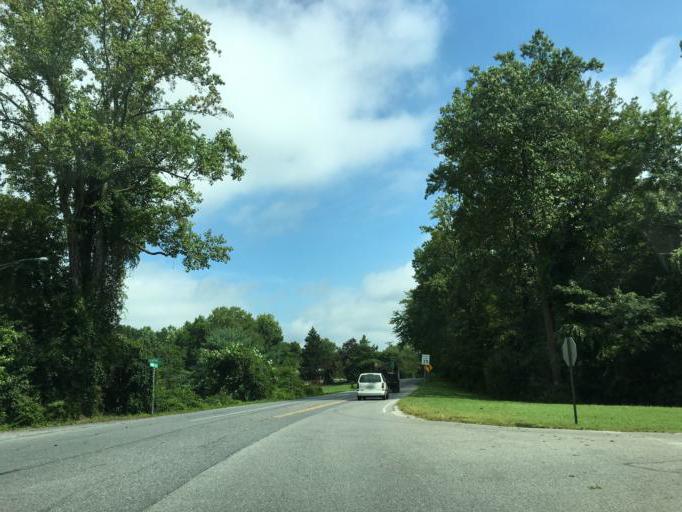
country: US
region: Maryland
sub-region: Anne Arundel County
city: Crownsville
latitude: 39.0143
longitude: -76.5968
